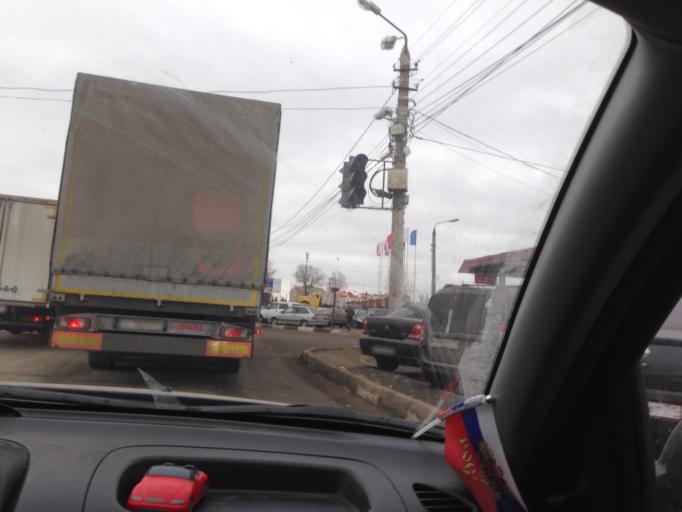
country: RU
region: Tula
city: Tula
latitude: 54.1662
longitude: 37.6410
